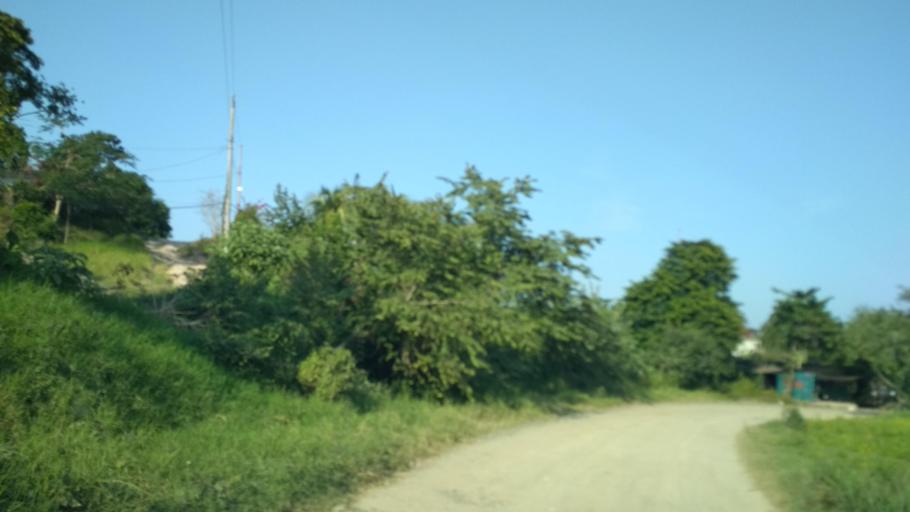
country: MX
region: Puebla
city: San Jose Acateno
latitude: 20.2186
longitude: -97.2635
